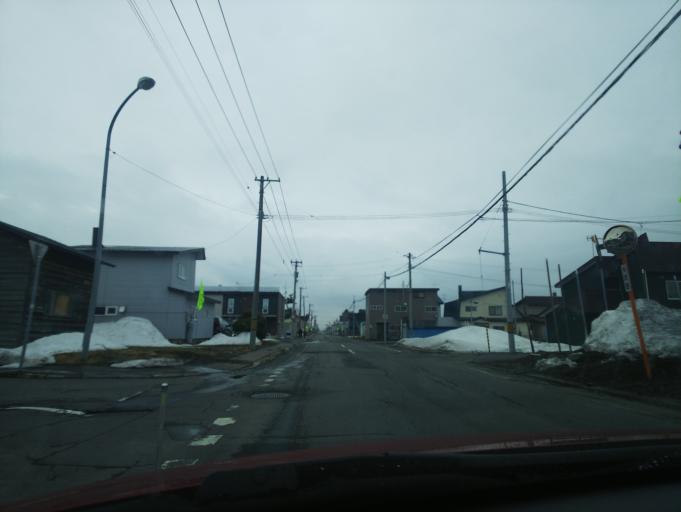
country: JP
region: Hokkaido
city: Nayoro
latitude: 44.3640
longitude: 142.4502
